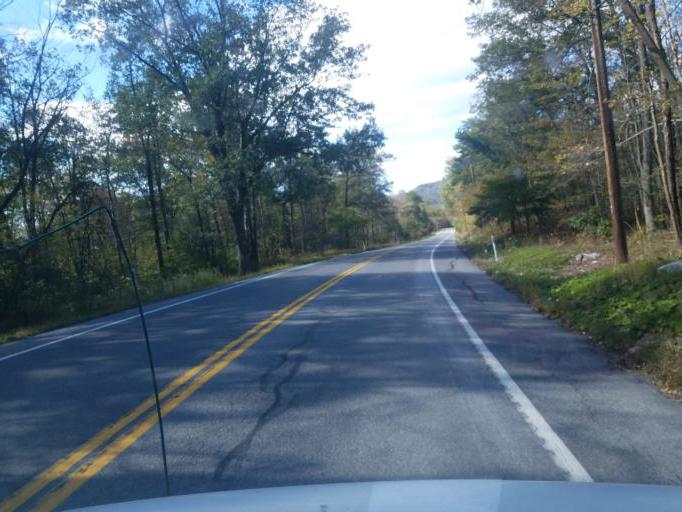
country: US
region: Pennsylvania
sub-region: Bedford County
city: Earlston
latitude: 40.0211
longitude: -78.1743
